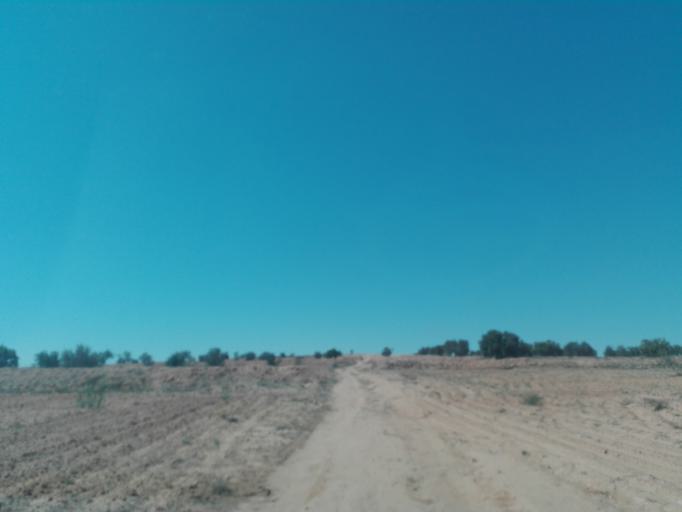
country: TN
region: Safaqis
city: Bi'r `Ali Bin Khalifah
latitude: 34.7961
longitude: 10.2837
